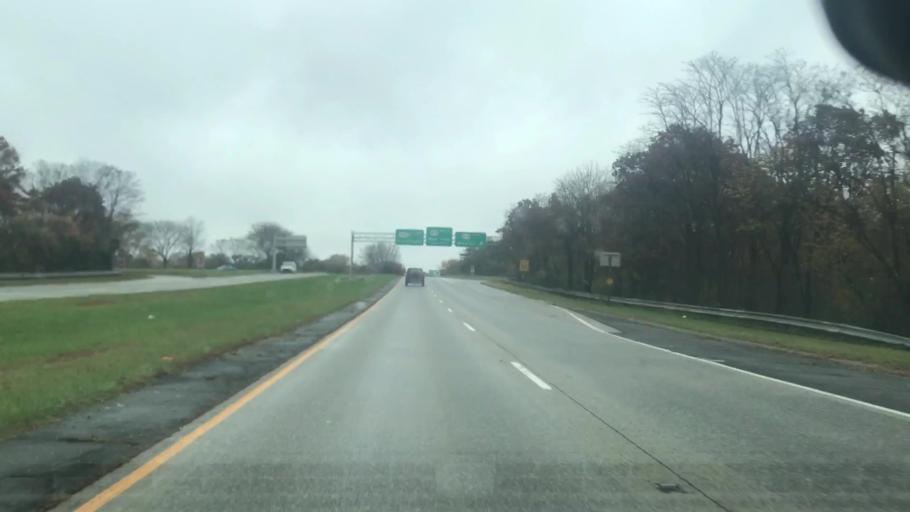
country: US
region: New York
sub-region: Suffolk County
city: North Babylon
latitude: 40.7153
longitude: -73.3140
